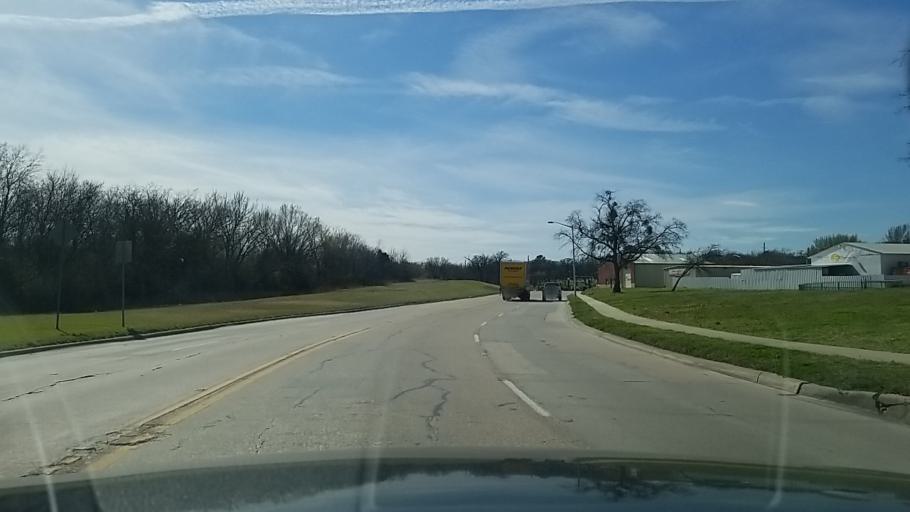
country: US
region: Texas
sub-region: Denton County
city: Denton
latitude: 33.2087
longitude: -97.1304
